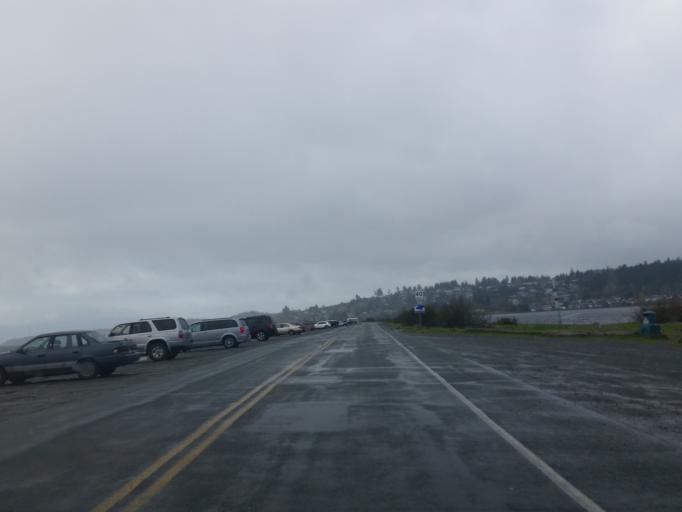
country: CA
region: British Columbia
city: Colwood
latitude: 48.4298
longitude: -123.4579
